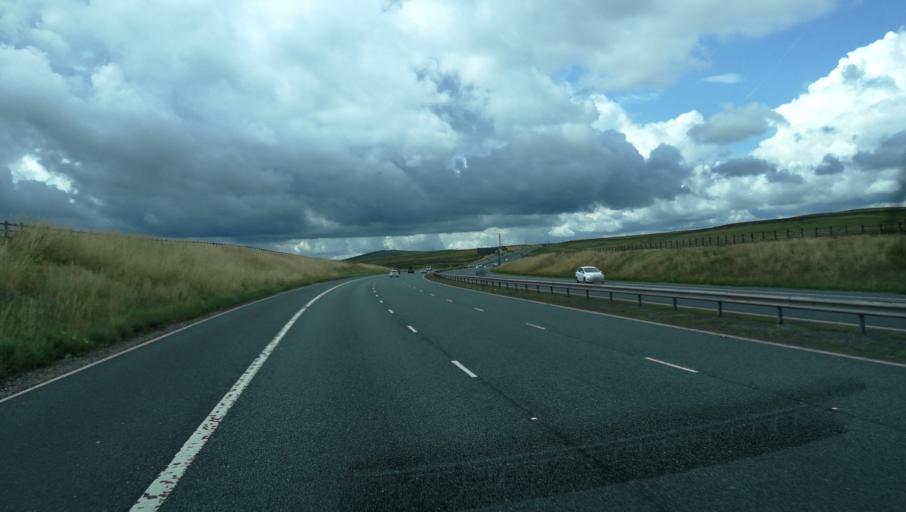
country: GB
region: Scotland
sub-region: South Lanarkshire
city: Douglas
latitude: 55.5209
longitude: -3.7416
